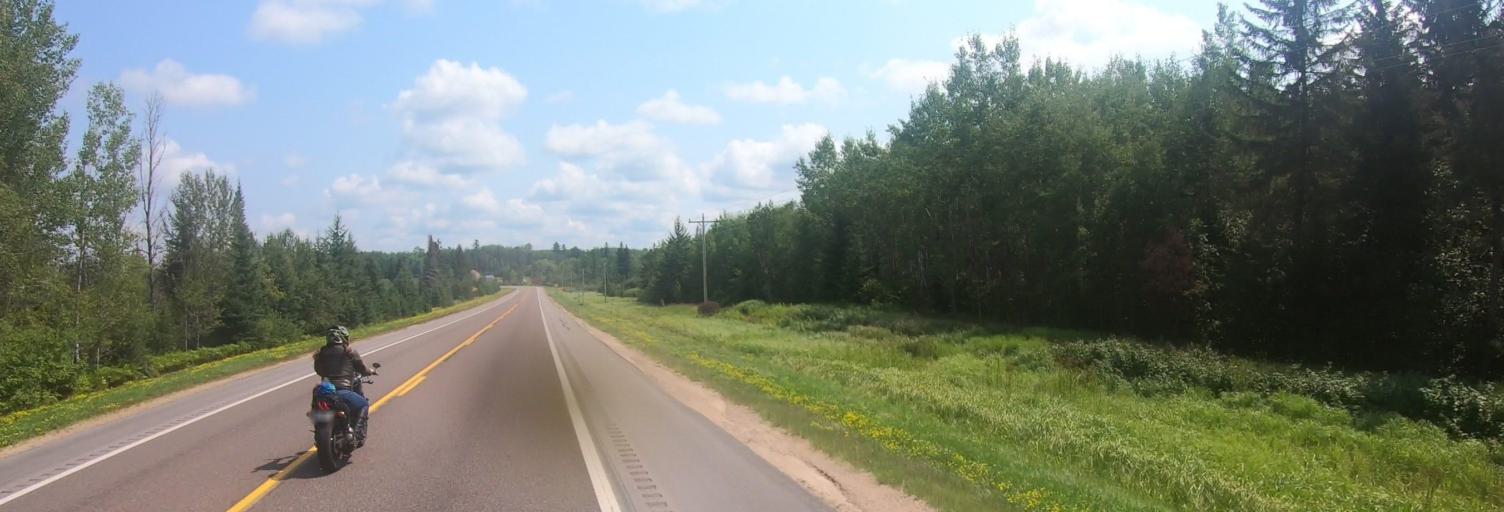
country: US
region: Minnesota
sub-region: Saint Louis County
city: Parkville
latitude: 48.1208
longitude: -92.5322
